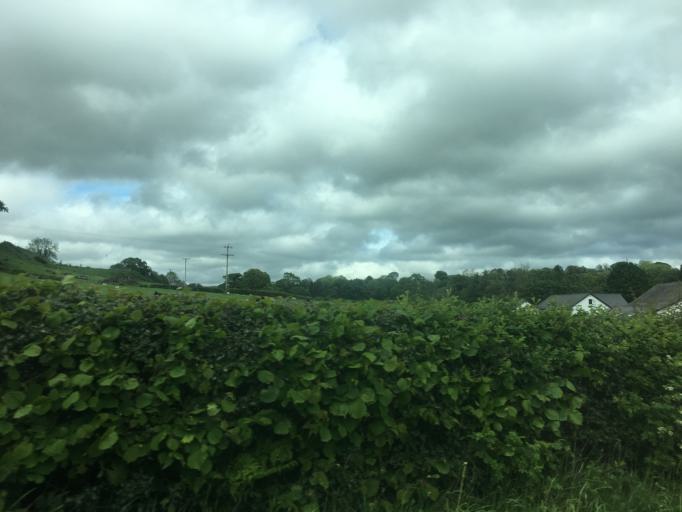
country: GB
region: Wales
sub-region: Carmarthenshire
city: Llansawel
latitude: 52.0728
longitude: -3.9963
